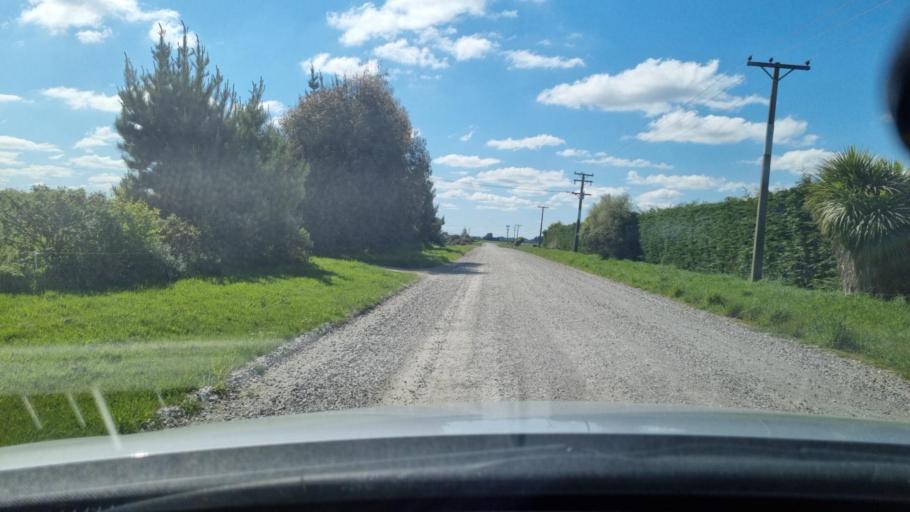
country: NZ
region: Southland
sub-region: Invercargill City
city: Invercargill
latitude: -46.3728
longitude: 168.2985
